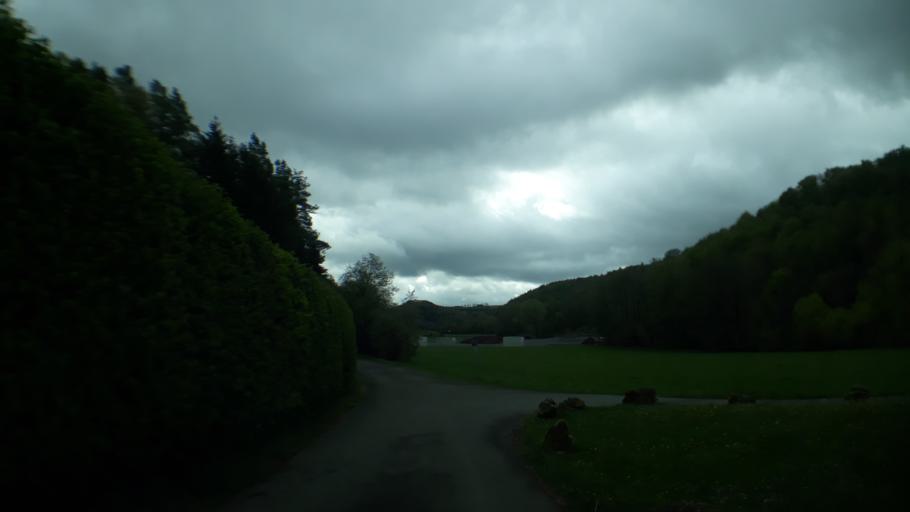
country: DE
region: North Rhine-Westphalia
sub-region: Regierungsbezirk Koln
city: Nettersheim
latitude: 50.5142
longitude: 6.6137
